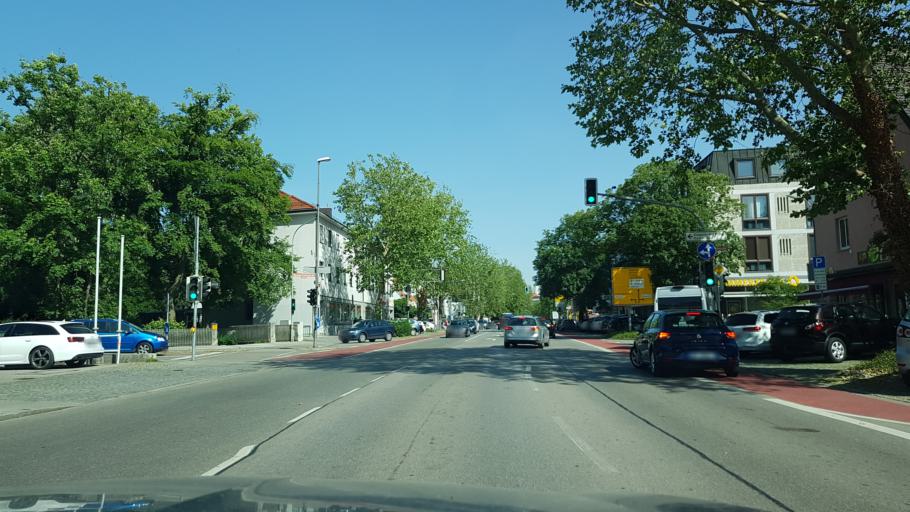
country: DE
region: Bavaria
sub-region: Upper Bavaria
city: Dachau
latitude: 48.2518
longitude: 11.4417
